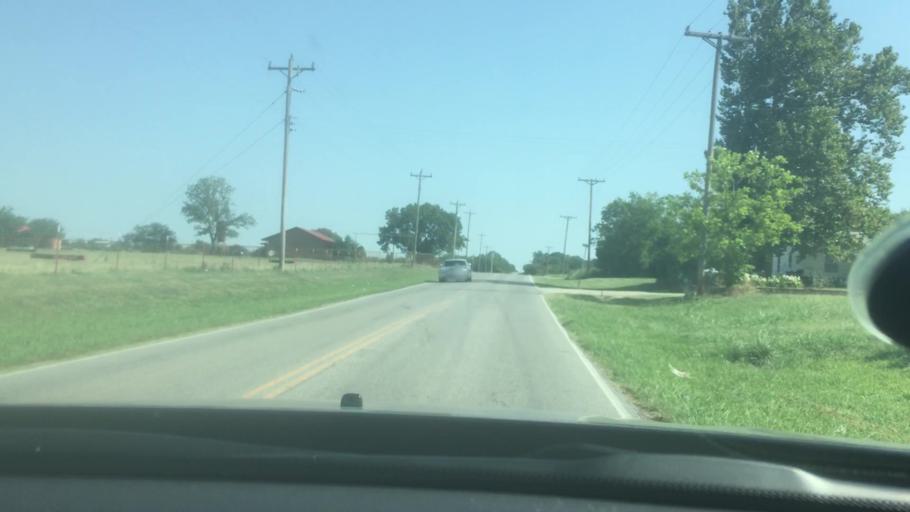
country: US
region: Oklahoma
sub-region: Bryan County
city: Calera
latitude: 34.0052
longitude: -96.4656
